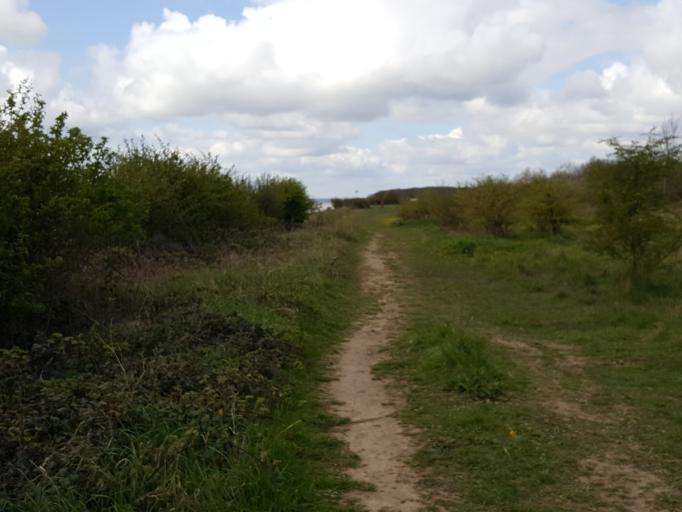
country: GB
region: England
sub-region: East Riding of Yorkshire
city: North Ferriby
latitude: 53.7160
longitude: -0.4919
